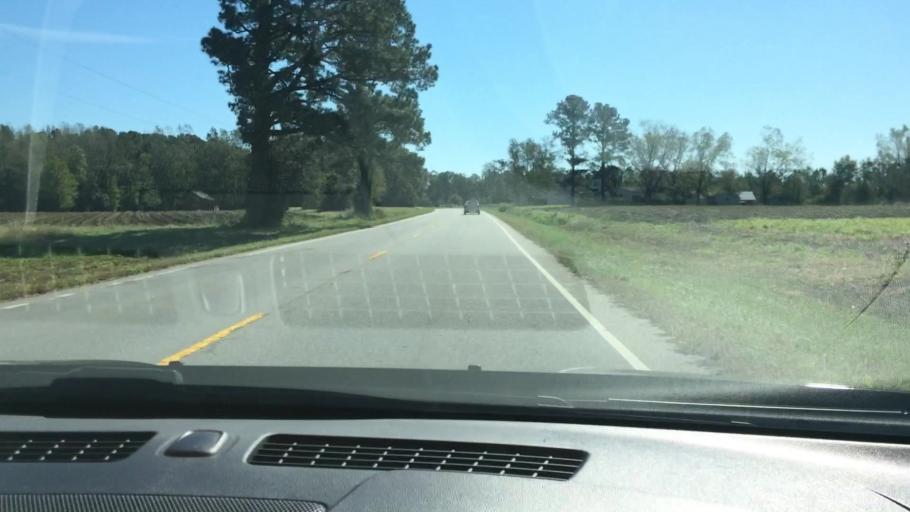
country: US
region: North Carolina
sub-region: Pitt County
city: Grifton
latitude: 35.3578
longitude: -77.3419
